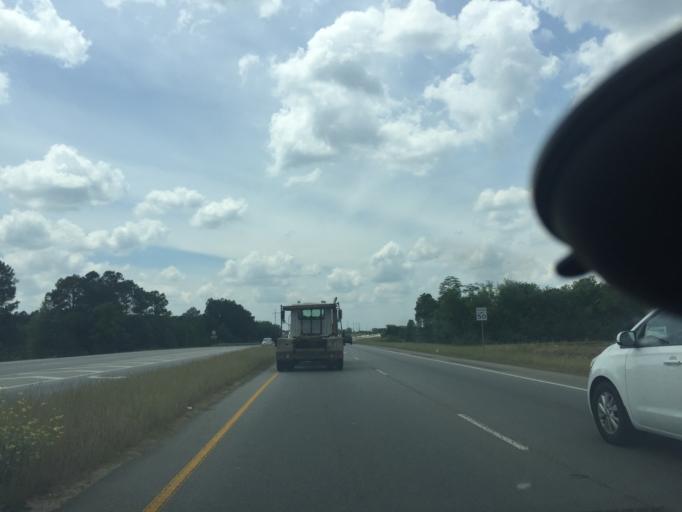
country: US
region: Georgia
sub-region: Bulloch County
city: Statesboro
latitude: 32.4059
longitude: -81.7705
